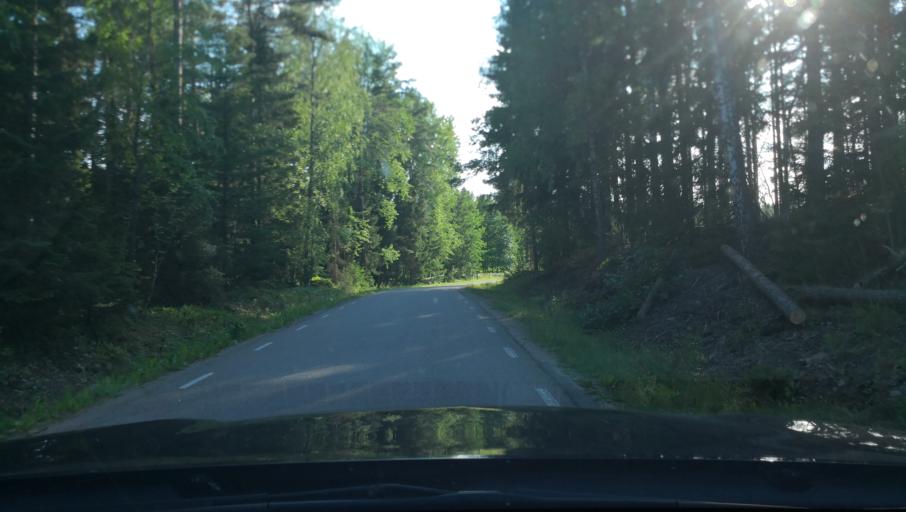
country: SE
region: Uppsala
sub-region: Osthammars Kommun
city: Osterbybruk
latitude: 60.0174
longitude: 17.9357
